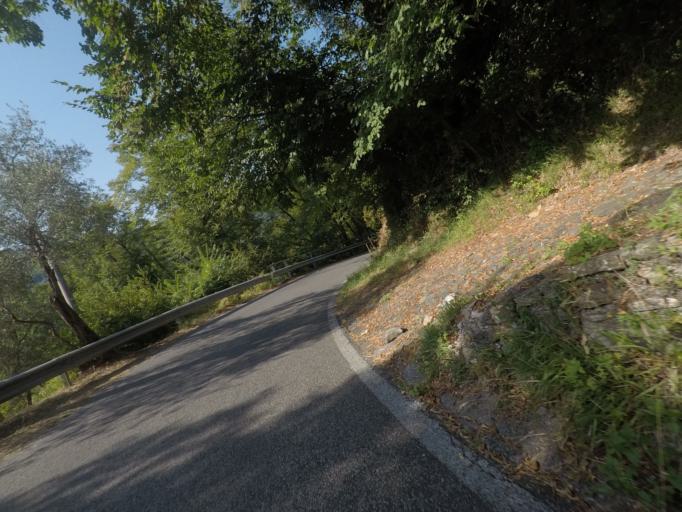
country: IT
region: Liguria
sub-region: Provincia di La Spezia
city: Casano-Dogana-Isola
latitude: 44.0874
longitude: 10.0496
